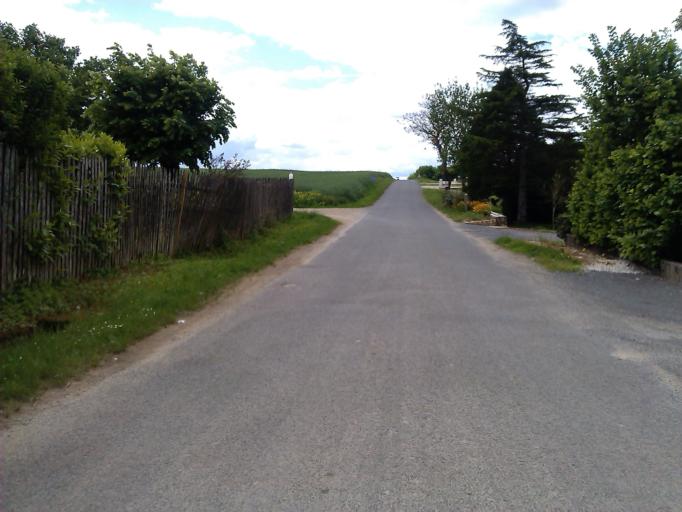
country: FR
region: Poitou-Charentes
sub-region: Departement de la Charente
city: Nanteuil-en-Vallee
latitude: 45.9572
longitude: 0.2516
